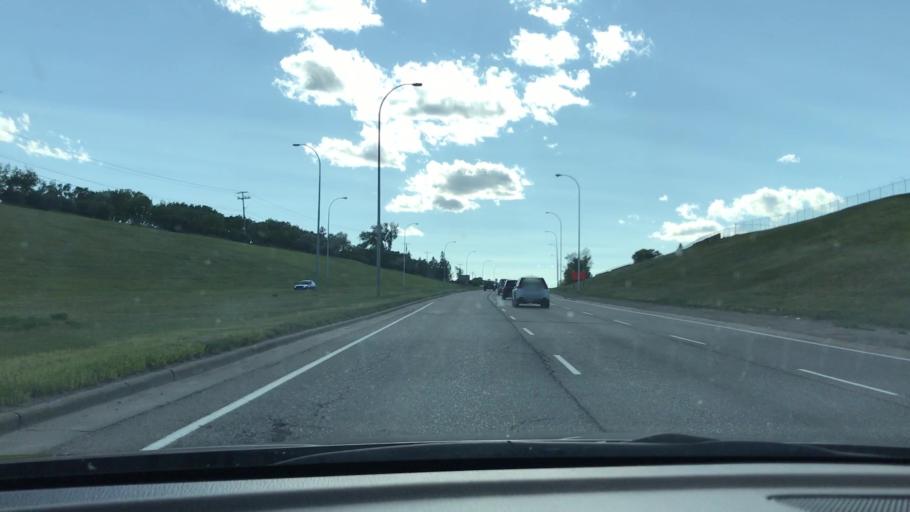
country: CA
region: Alberta
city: Calgary
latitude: 51.0670
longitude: -114.0318
